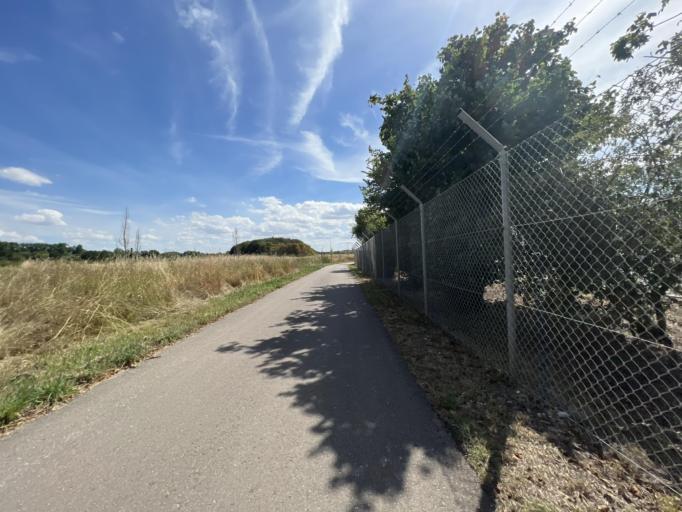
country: DE
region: North Rhine-Westphalia
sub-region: Regierungsbezirk Koln
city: Niederzier
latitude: 50.8454
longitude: 6.4353
